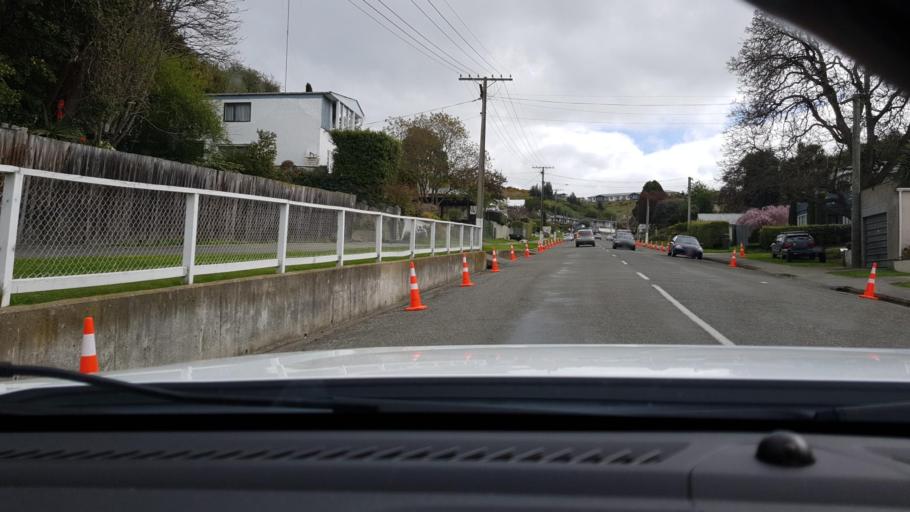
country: NZ
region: Otago
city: Oamaru
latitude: -45.0947
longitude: 170.9641
